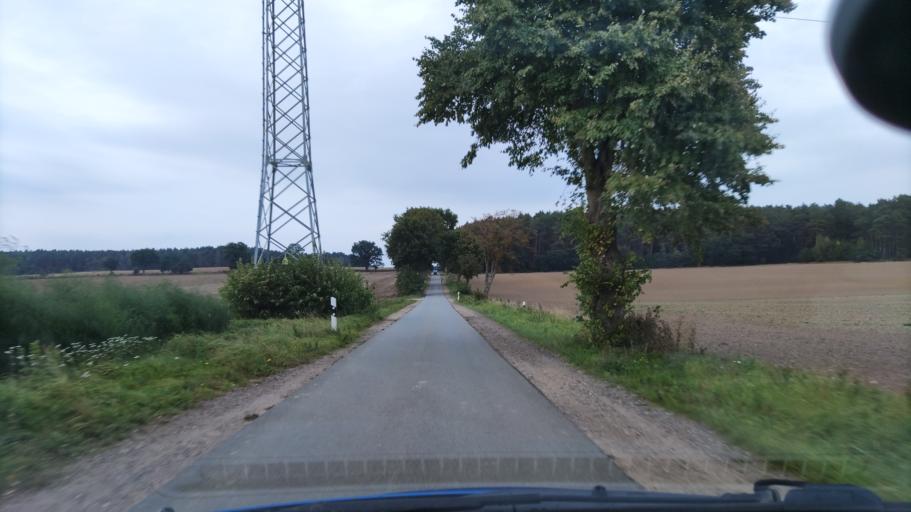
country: DE
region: Lower Saxony
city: Karwitz
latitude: 53.0966
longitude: 11.0151
